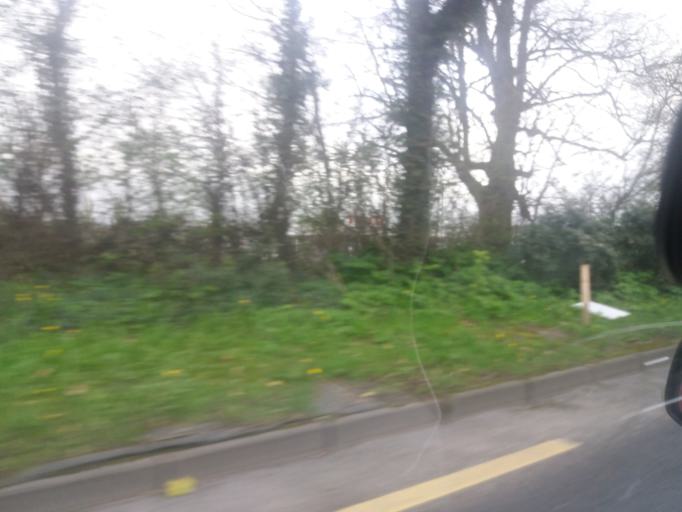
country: IE
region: Munster
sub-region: County Limerick
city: Newcastle West
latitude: 52.4507
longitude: -9.0473
